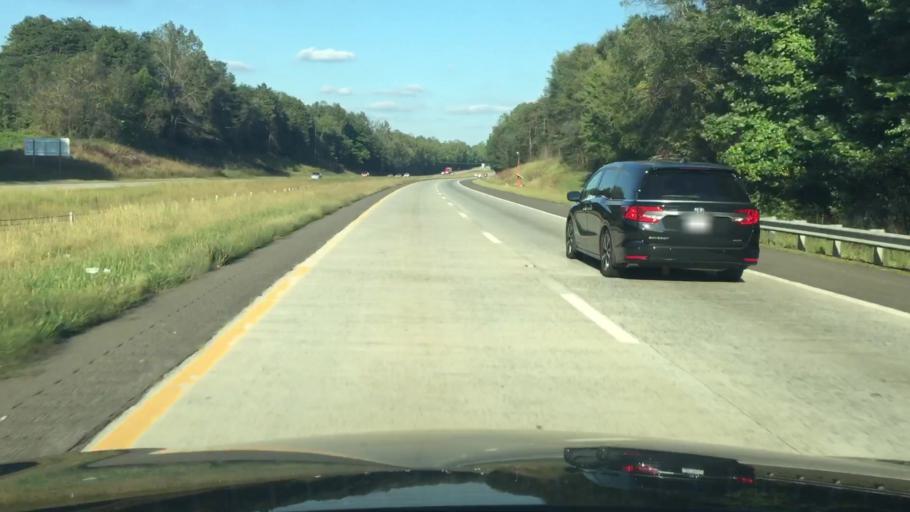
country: US
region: North Carolina
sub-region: Davie County
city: Mocksville
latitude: 35.8795
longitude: -80.6876
